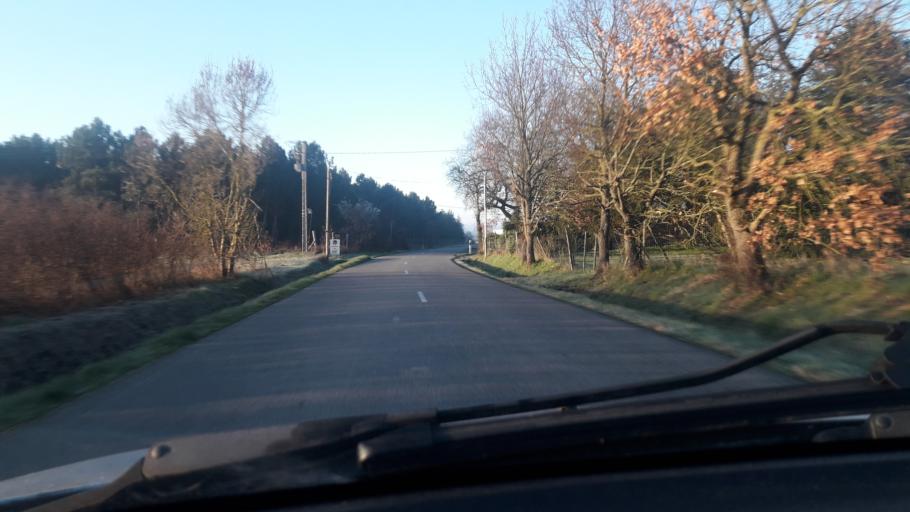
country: FR
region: Midi-Pyrenees
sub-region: Departement de la Haute-Garonne
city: Longages
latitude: 43.3491
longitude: 1.2130
